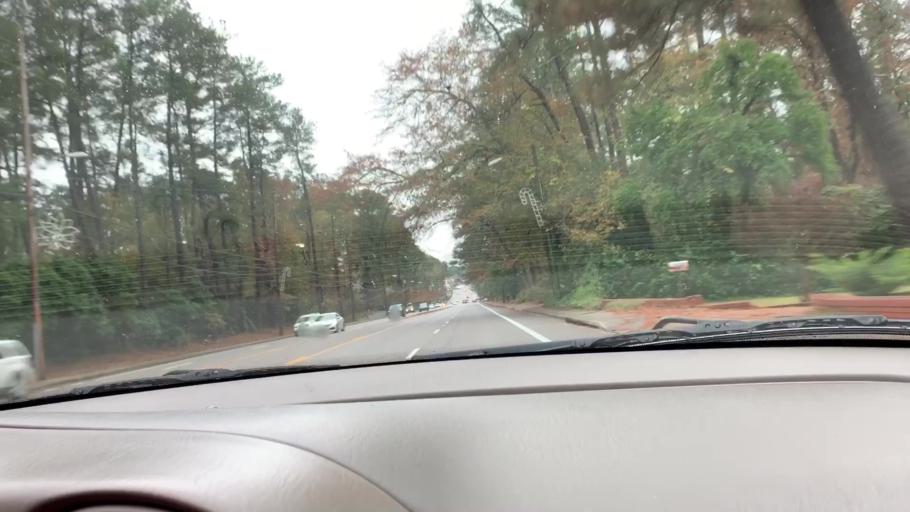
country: US
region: South Carolina
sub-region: Richland County
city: Forest Acres
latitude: 34.0262
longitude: -80.9664
